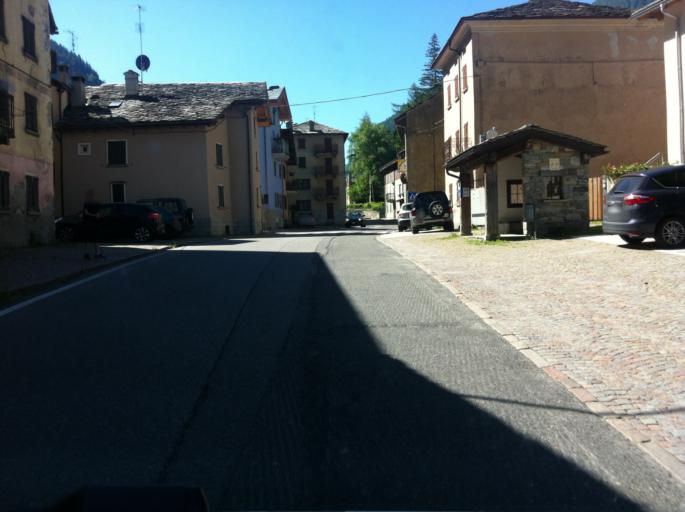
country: IT
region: Lombardy
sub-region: Provincia di Sondrio
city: Campodolcino
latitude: 46.4153
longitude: 9.3428
